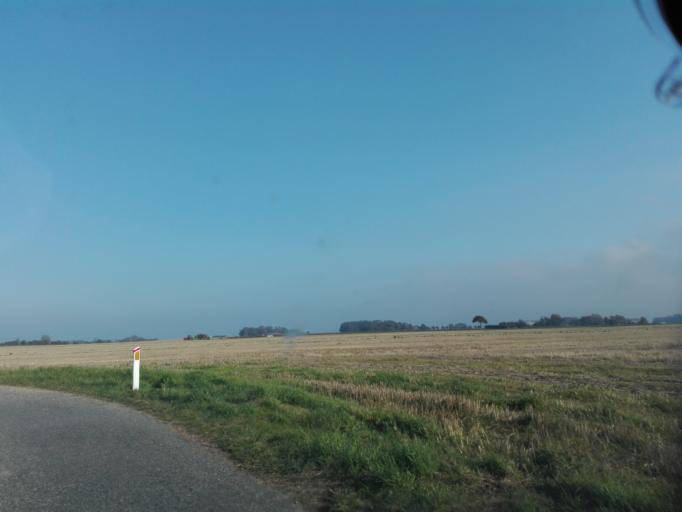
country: DK
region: Central Jutland
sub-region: Odder Kommune
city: Odder
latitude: 55.8832
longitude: 10.1656
